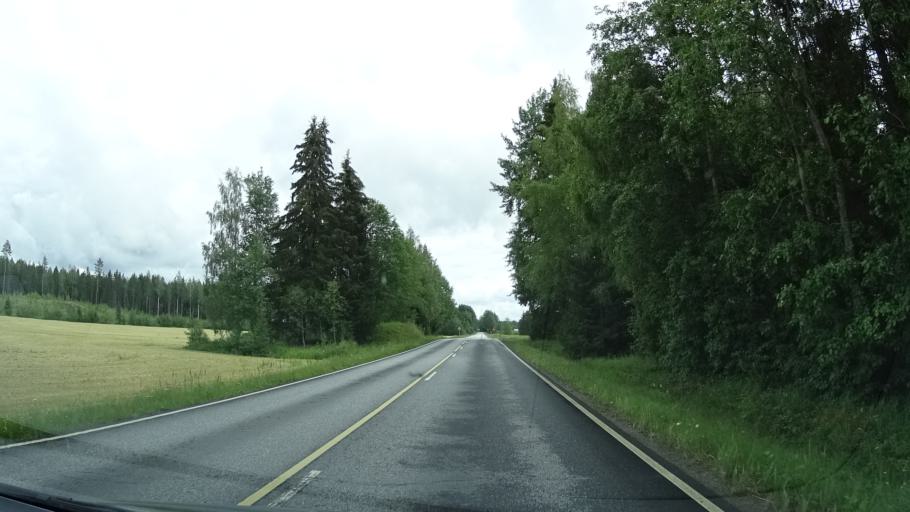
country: FI
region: Haeme
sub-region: Forssa
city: Humppila
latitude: 61.0958
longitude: 23.3599
